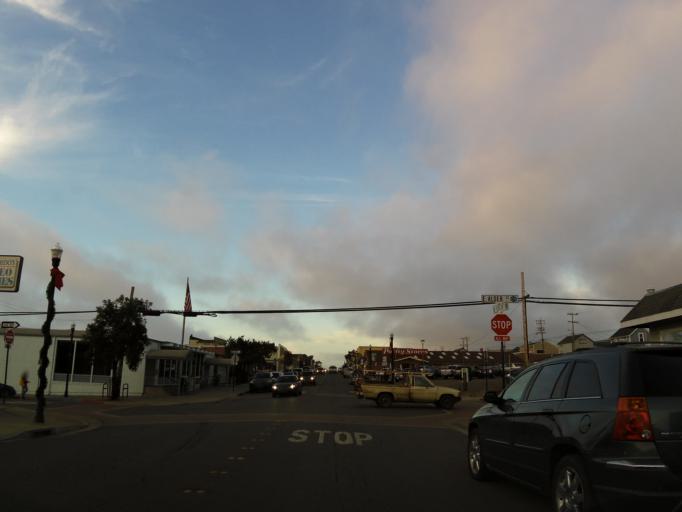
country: US
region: California
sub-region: Mendocino County
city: Fort Bragg
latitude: 39.4427
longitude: -123.8046
